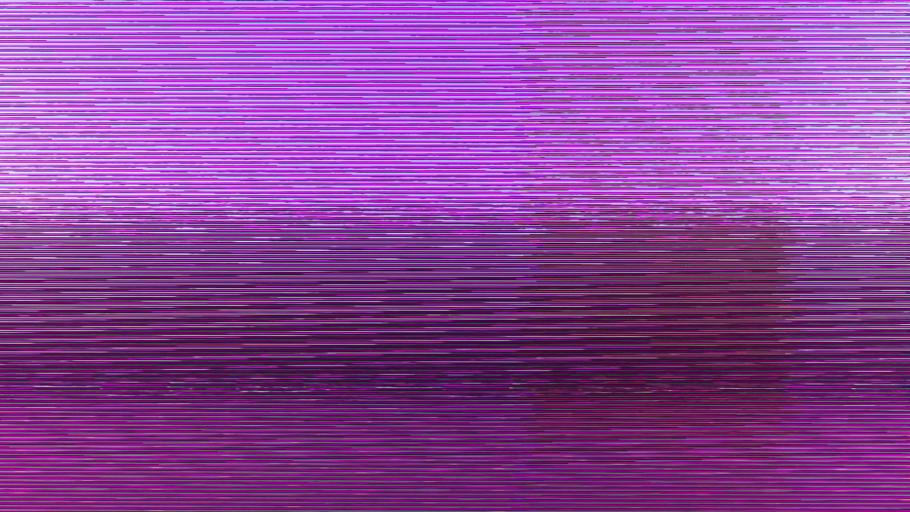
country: US
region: Michigan
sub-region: Washtenaw County
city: Ann Arbor
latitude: 42.2886
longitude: -83.8198
